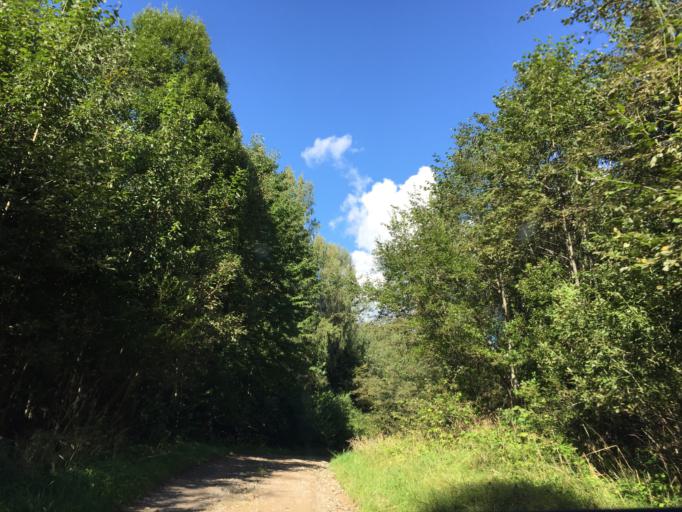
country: LV
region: Kuldigas Rajons
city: Kuldiga
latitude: 56.9749
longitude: 21.9083
